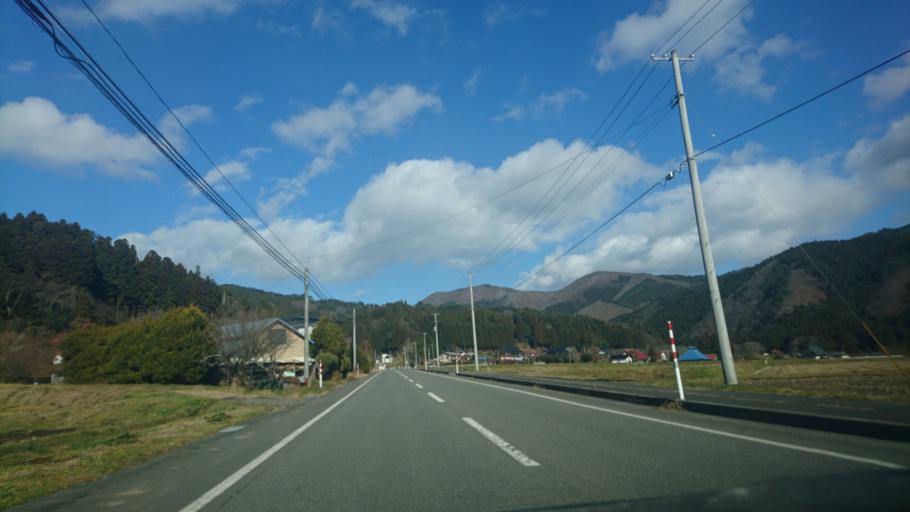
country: JP
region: Iwate
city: Mizusawa
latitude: 39.0712
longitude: 141.3815
